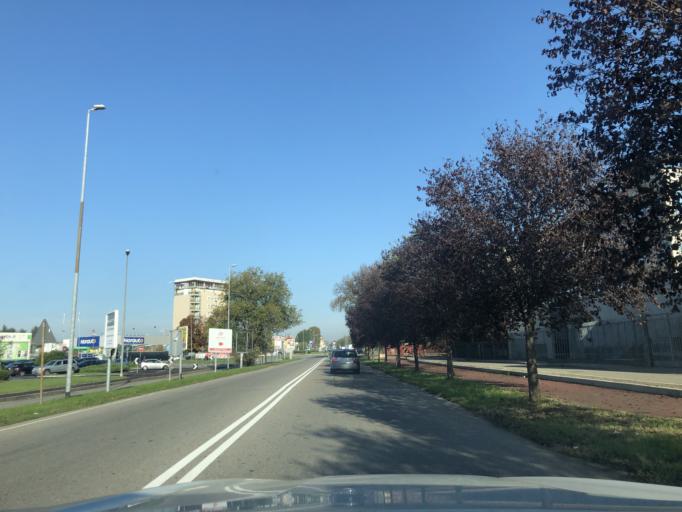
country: IT
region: Lombardy
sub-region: Citta metropolitana di Milano
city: Baranzate
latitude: 45.5323
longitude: 9.1081
